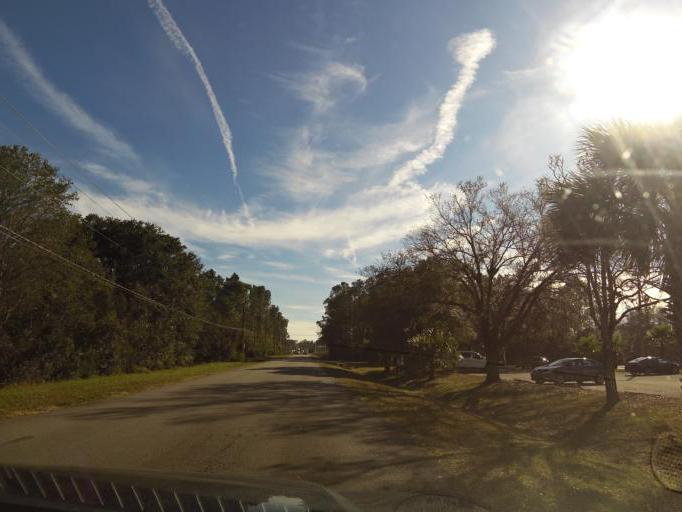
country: US
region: Florida
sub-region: Saint Johns County
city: Saint Augustine
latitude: 29.9197
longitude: -81.4033
